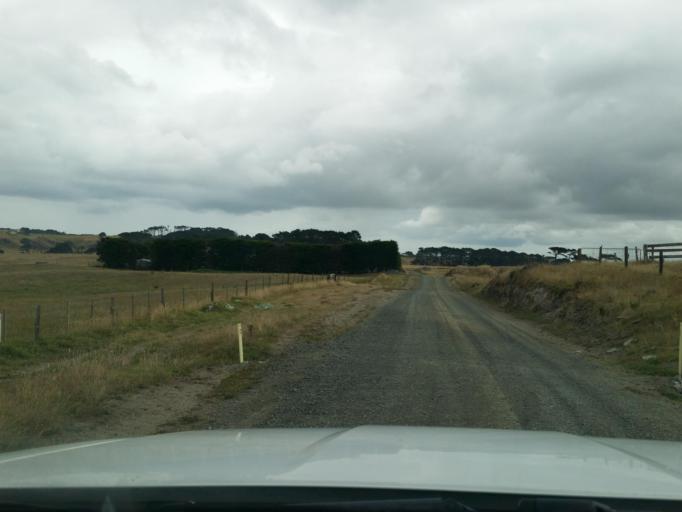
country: NZ
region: Northland
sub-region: Kaipara District
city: Dargaville
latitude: -35.9910
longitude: 173.8303
